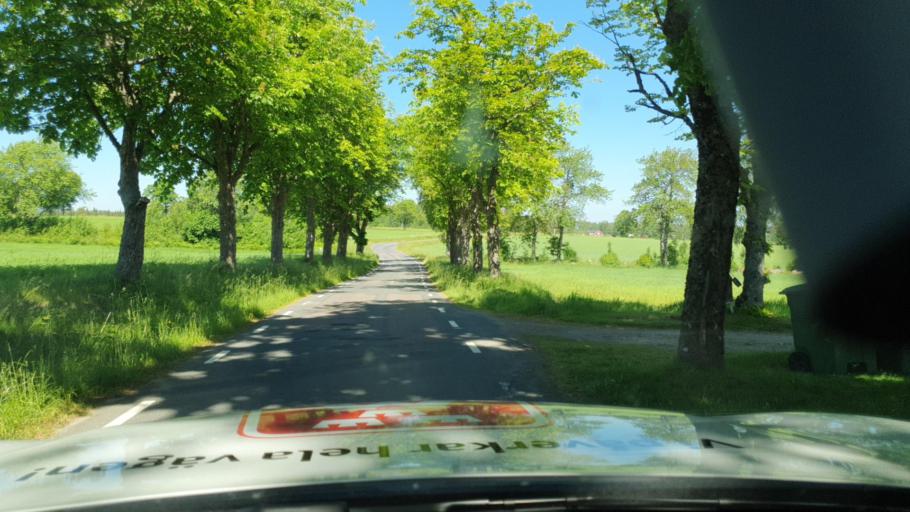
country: SE
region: Joenkoeping
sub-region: Habo Kommun
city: Habo
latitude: 57.9072
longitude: 14.0468
